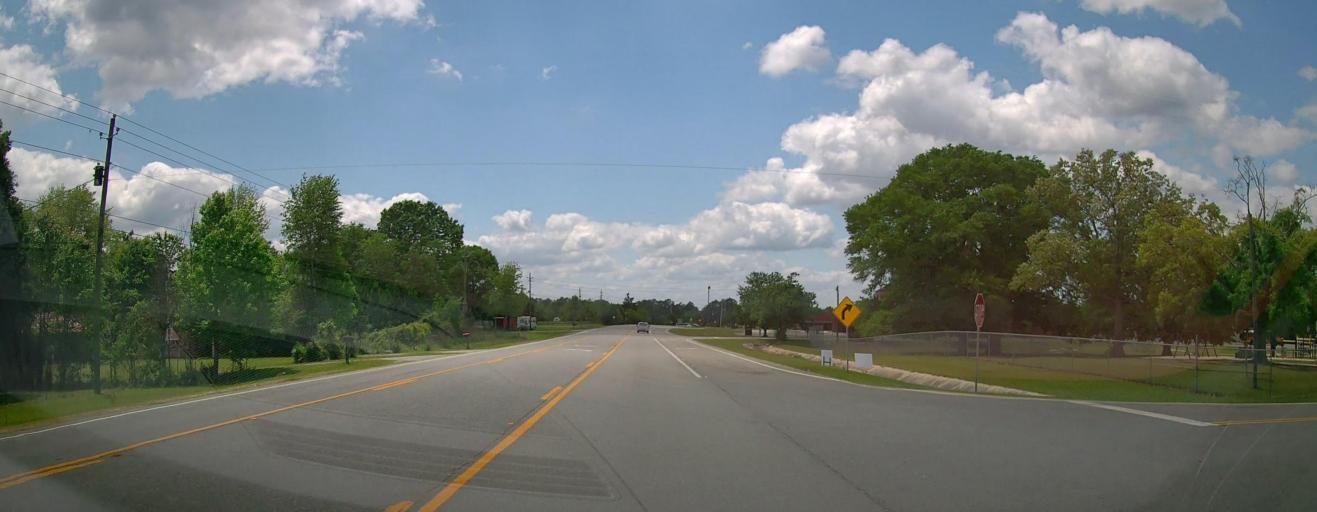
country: US
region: Georgia
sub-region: Laurens County
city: East Dublin
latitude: 32.5619
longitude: -82.8153
